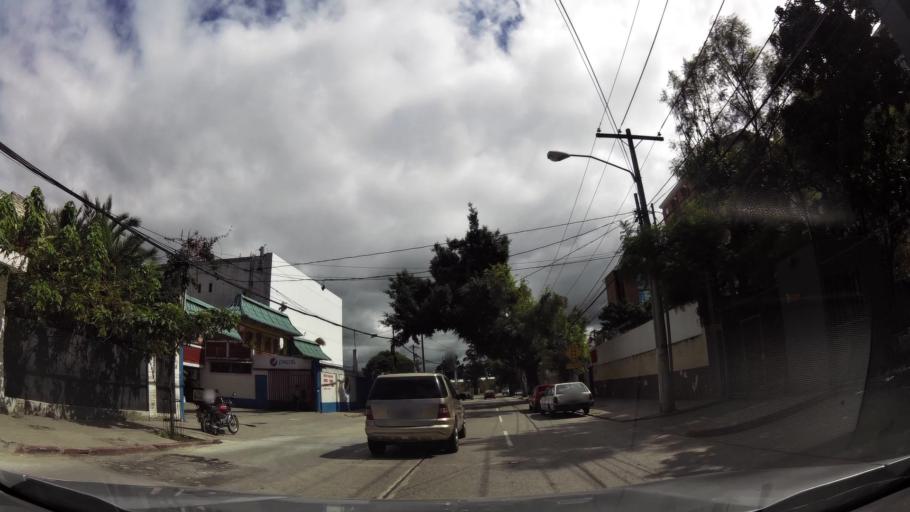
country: GT
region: Guatemala
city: Guatemala City
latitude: 14.6087
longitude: -90.5162
